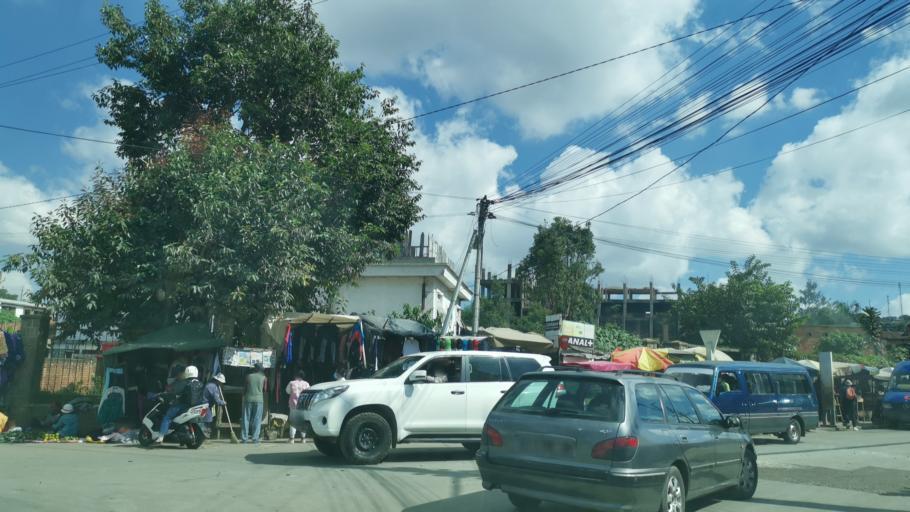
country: MG
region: Analamanga
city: Antananarivo
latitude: -18.9354
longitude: 47.5287
